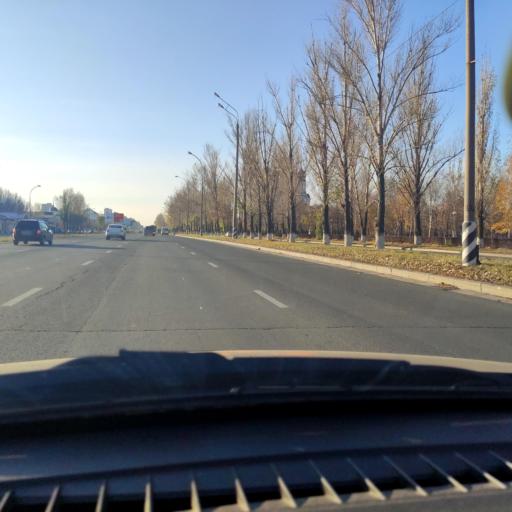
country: RU
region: Samara
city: Tol'yatti
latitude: 53.5240
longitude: 49.2802
